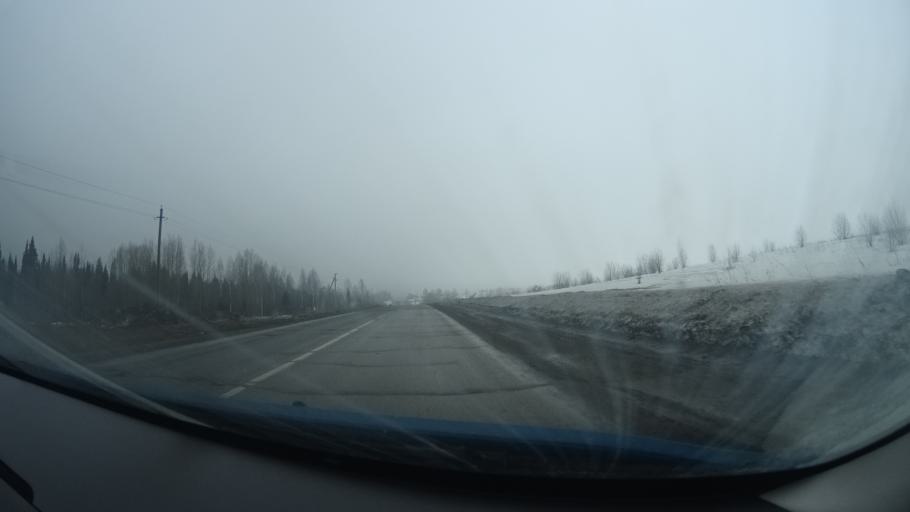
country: RU
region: Bashkortostan
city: Verkhniye Tatyshly
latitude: 56.4841
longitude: 55.7968
